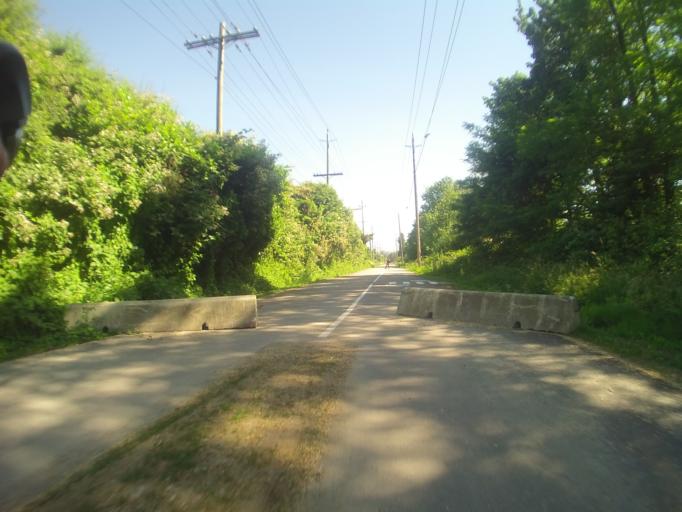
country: CA
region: British Columbia
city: Richmond
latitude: 49.2131
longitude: -123.1468
